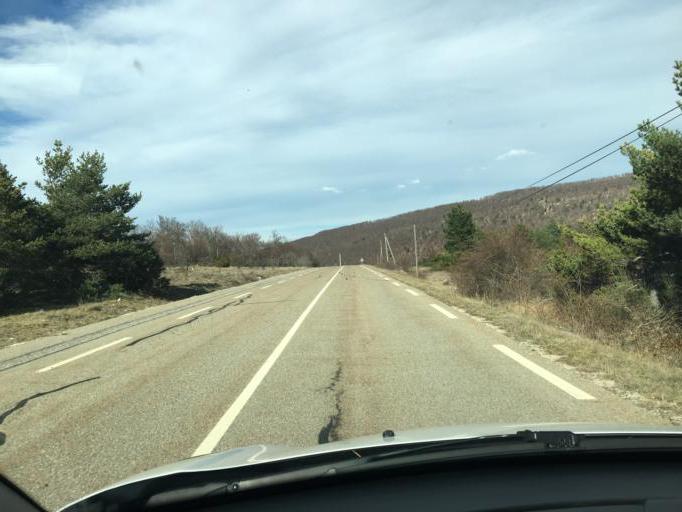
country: FR
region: Provence-Alpes-Cote d'Azur
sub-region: Departement du Vaucluse
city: Saint-Saturnin-les-Apt
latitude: 43.9785
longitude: 5.4703
